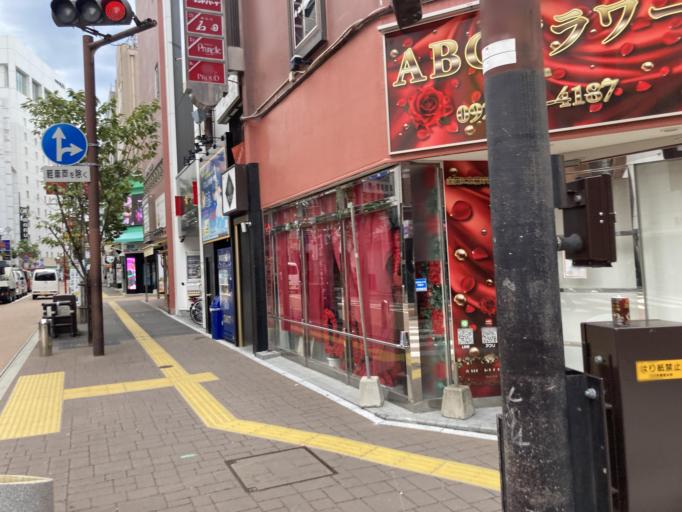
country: JP
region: Fukuoka
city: Fukuoka-shi
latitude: 33.5924
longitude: 130.4075
